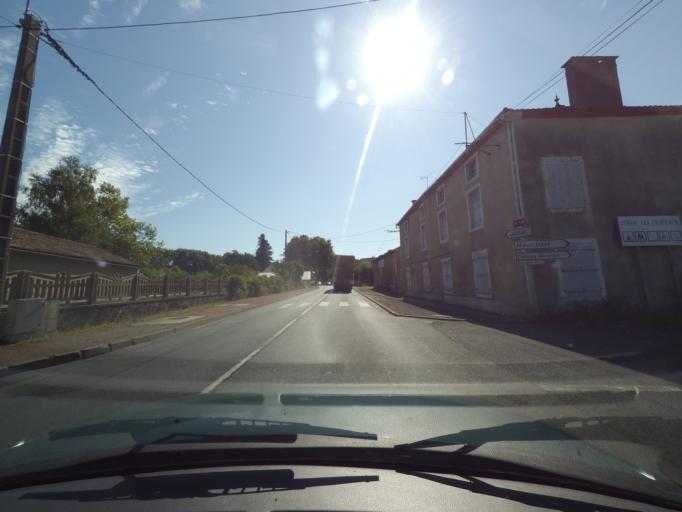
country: FR
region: Poitou-Charentes
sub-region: Departement de la Vienne
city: Lussac-les-Chateaux
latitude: 46.4043
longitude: 0.7050
